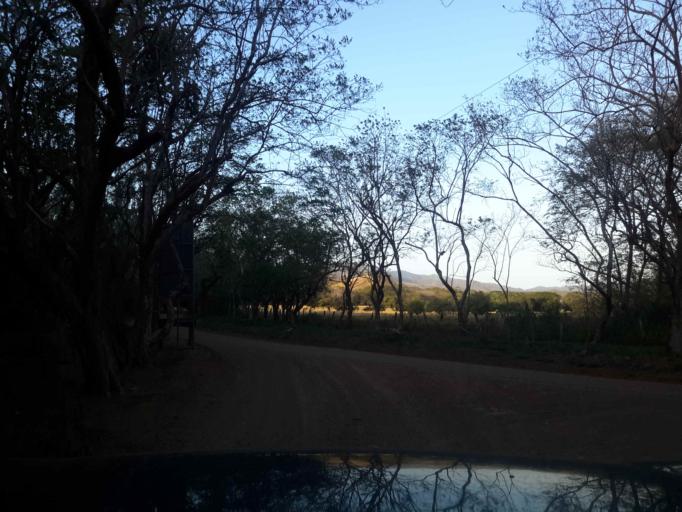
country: NI
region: Rivas
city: San Juan del Sur
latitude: 11.1909
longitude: -85.8112
